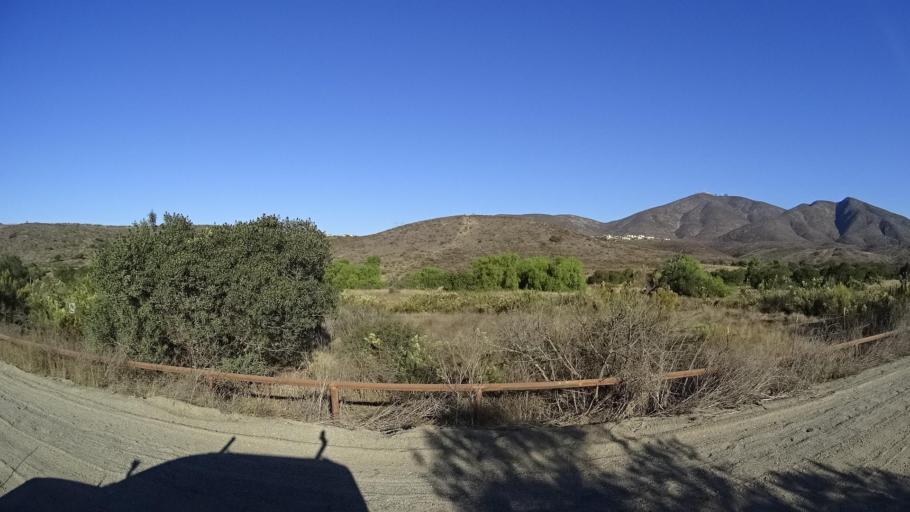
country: US
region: California
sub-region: San Diego County
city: Jamul
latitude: 32.6668
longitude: -116.9275
